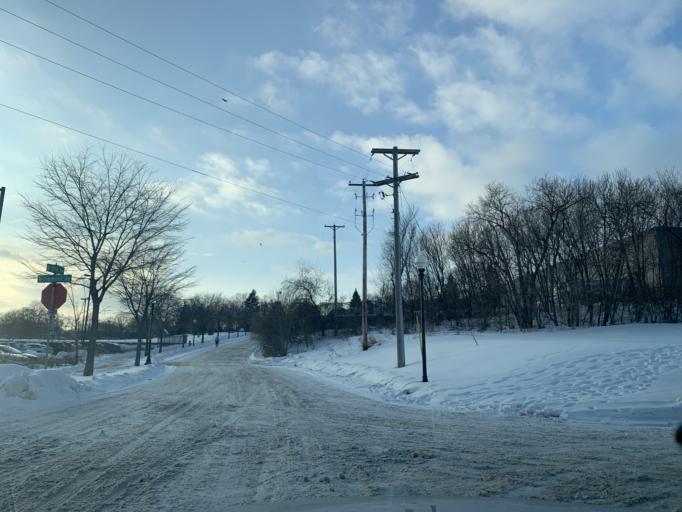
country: US
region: Minnesota
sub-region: Hennepin County
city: Minneapolis
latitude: 44.9882
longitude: -93.2956
